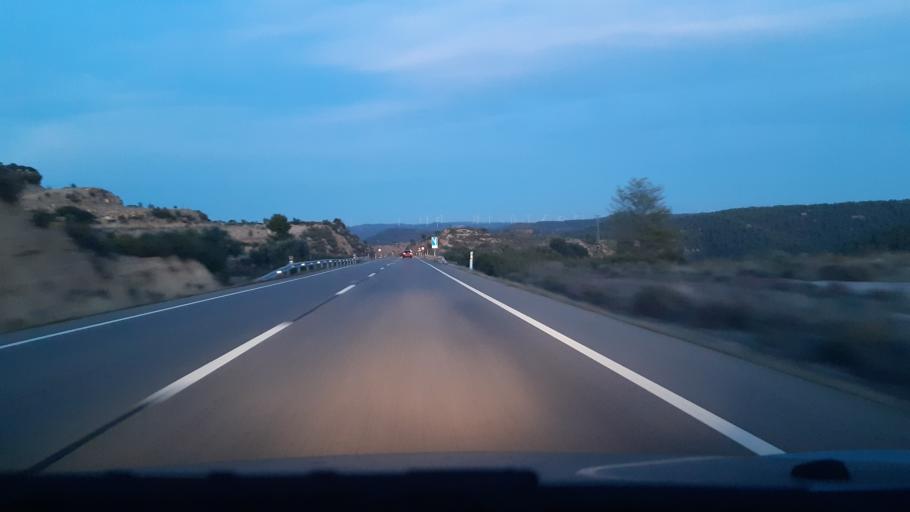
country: ES
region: Aragon
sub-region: Provincia de Teruel
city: Calaceite
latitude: 41.0204
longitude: 0.2122
